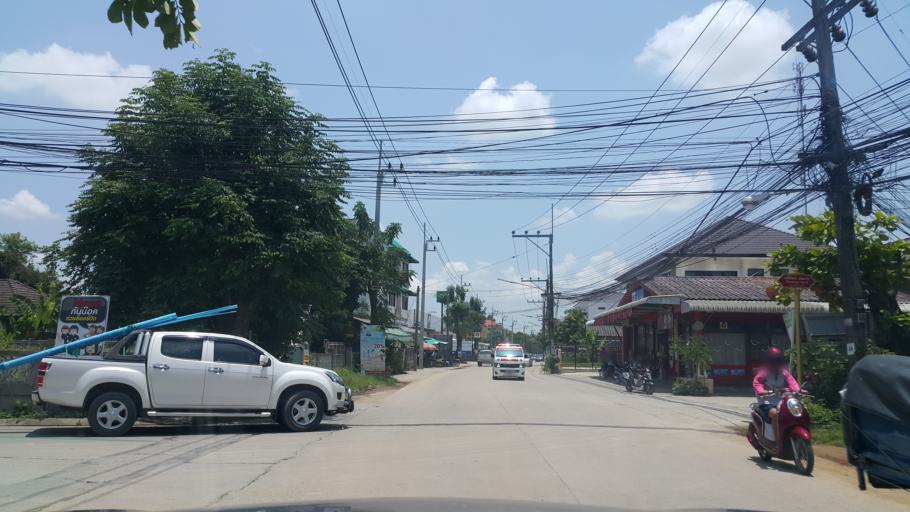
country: TH
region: Chiang Rai
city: Chiang Rai
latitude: 19.9296
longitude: 99.8156
